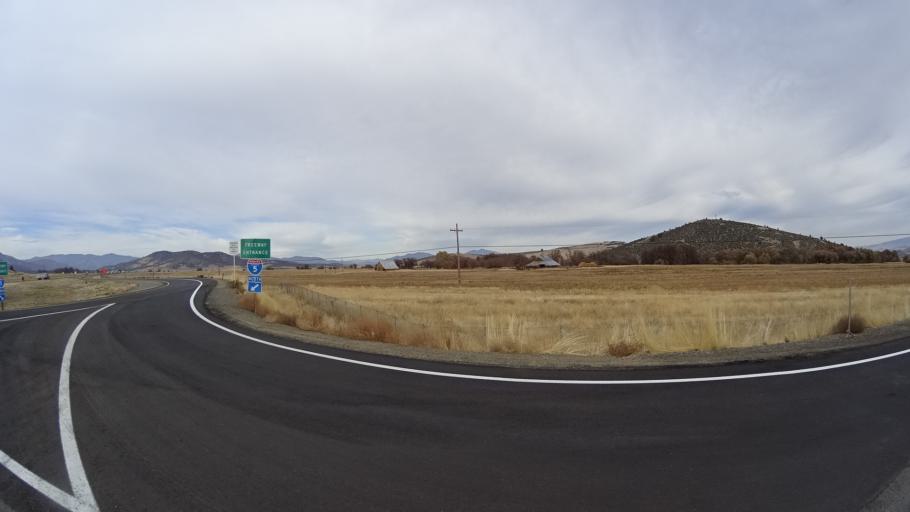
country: US
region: California
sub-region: Siskiyou County
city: Montague
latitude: 41.6468
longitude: -122.5331
